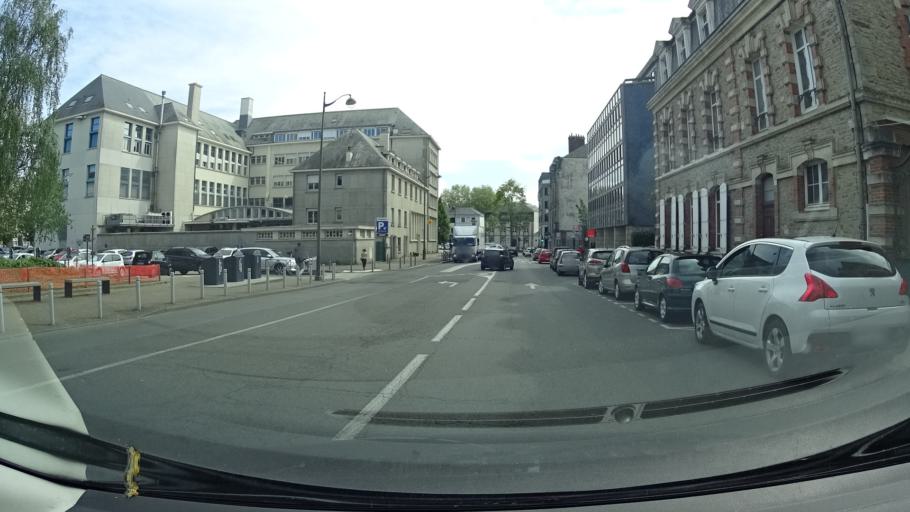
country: FR
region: Brittany
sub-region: Departement du Morbihan
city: Vannes
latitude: 47.6557
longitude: -2.7613
